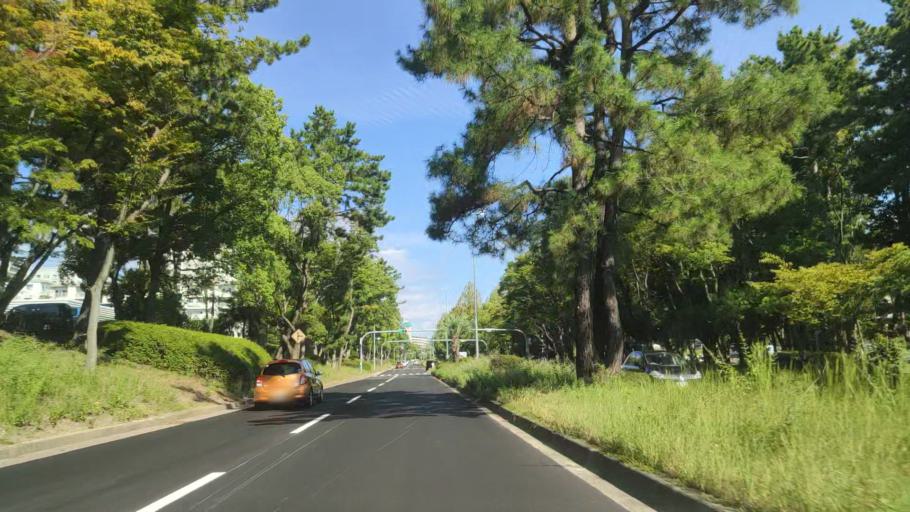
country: JP
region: Osaka
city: Suita
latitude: 34.7960
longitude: 135.5068
